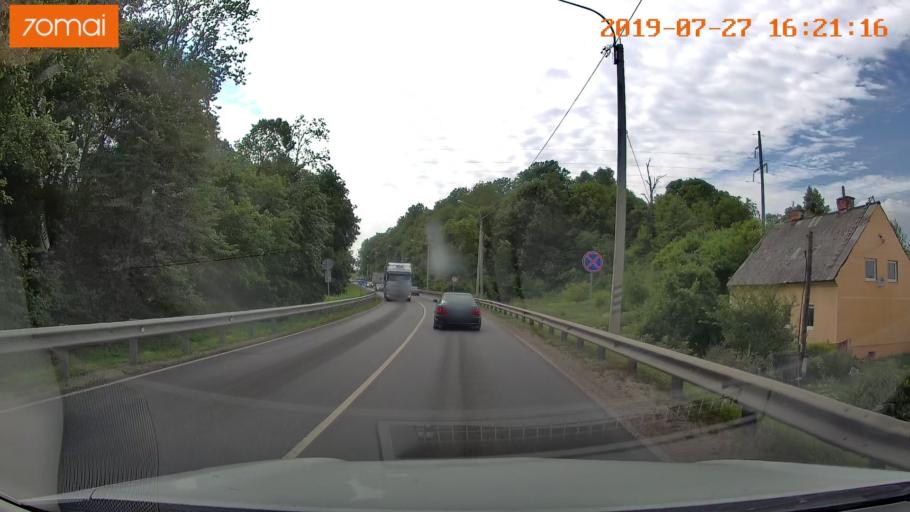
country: RU
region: Kaliningrad
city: Chernyakhovsk
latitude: 54.6266
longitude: 21.5167
